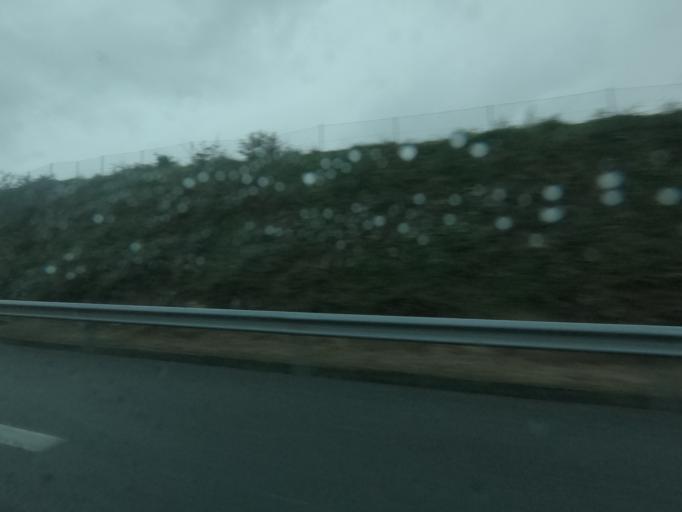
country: ES
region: Galicia
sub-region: Provincia de Pontevedra
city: Pontevedra
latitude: 42.3814
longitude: -8.6374
